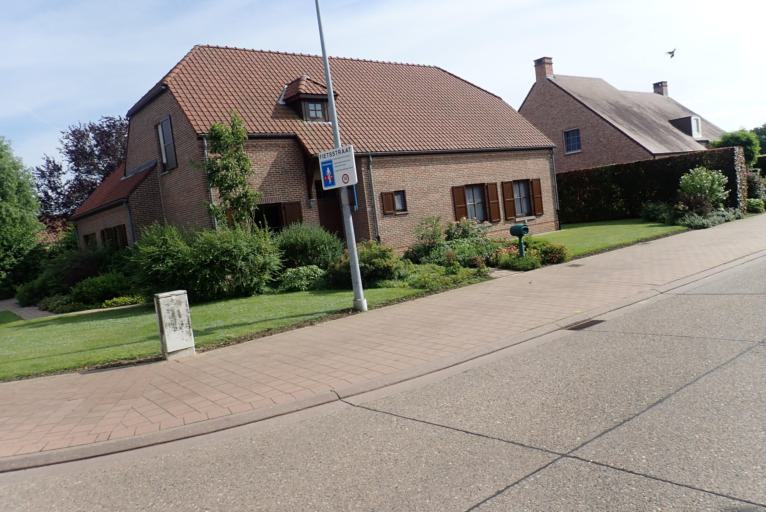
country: BE
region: Flanders
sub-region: Provincie Antwerpen
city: Heist-op-den-Berg
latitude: 51.0750
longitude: 4.7047
